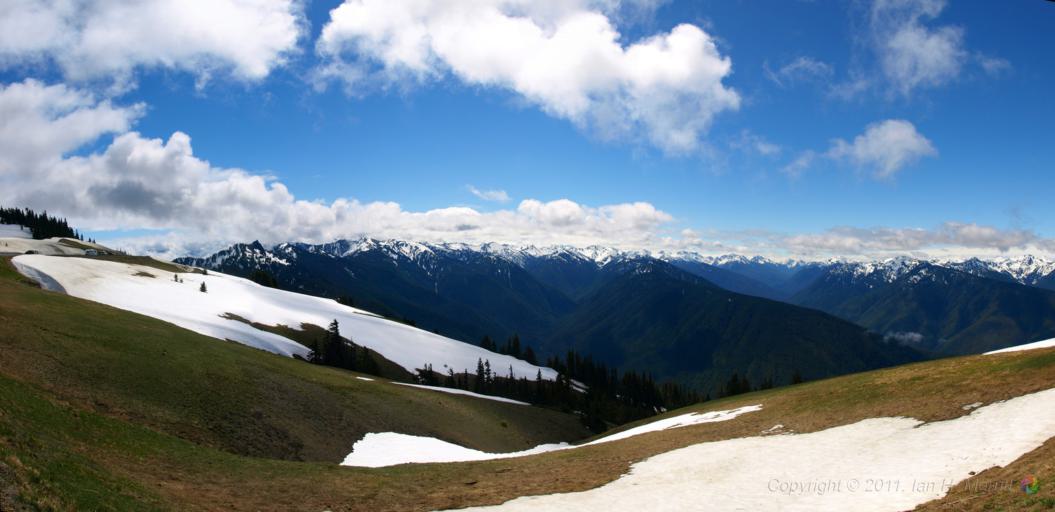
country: US
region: Washington
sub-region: Clallam County
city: Port Angeles
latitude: 47.9697
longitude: -123.4949
